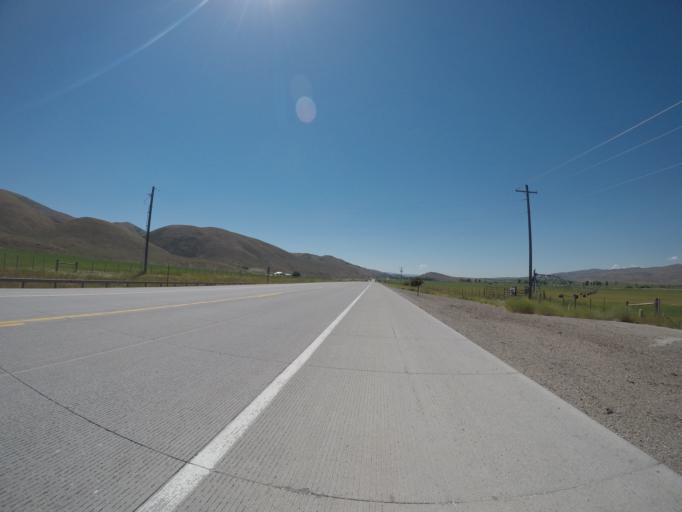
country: US
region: Idaho
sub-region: Bear Lake County
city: Montpelier
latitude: 42.1567
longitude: -110.9836
